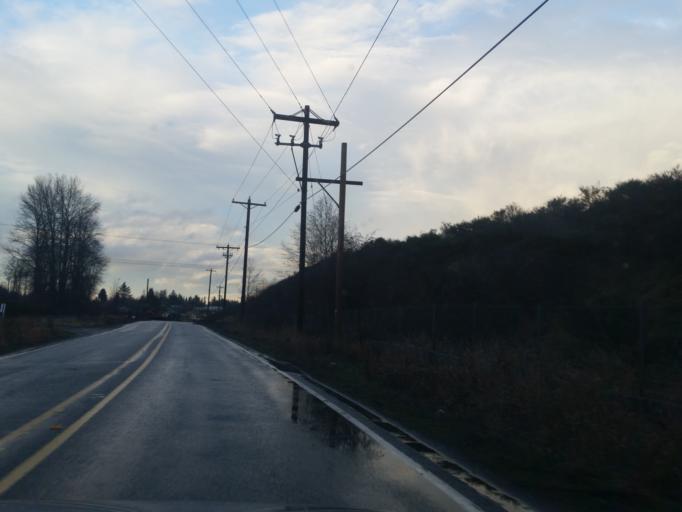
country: US
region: Washington
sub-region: Snohomish County
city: Maltby
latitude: 47.8052
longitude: -122.1116
